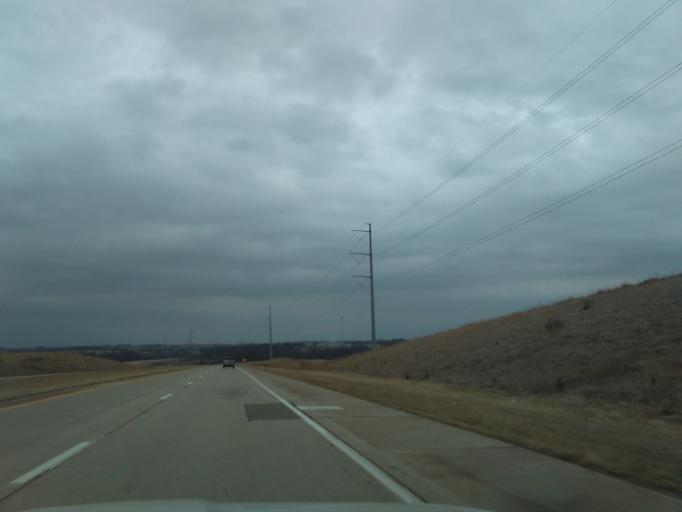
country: US
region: Nebraska
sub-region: Otoe County
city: Syracuse
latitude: 40.6755
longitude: -96.0496
